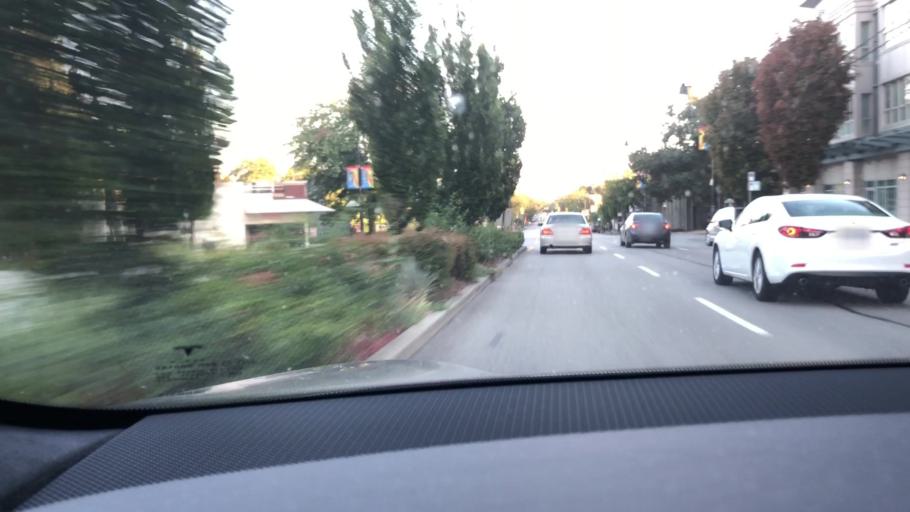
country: CA
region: British Columbia
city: Vancouver
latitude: 49.2519
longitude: -123.0793
